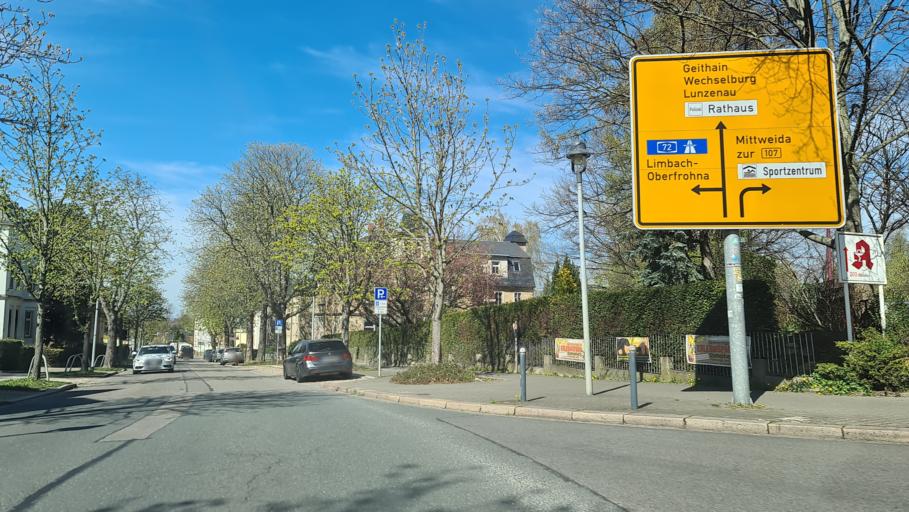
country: DE
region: Saxony
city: Burgstadt
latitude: 50.9163
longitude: 12.8122
